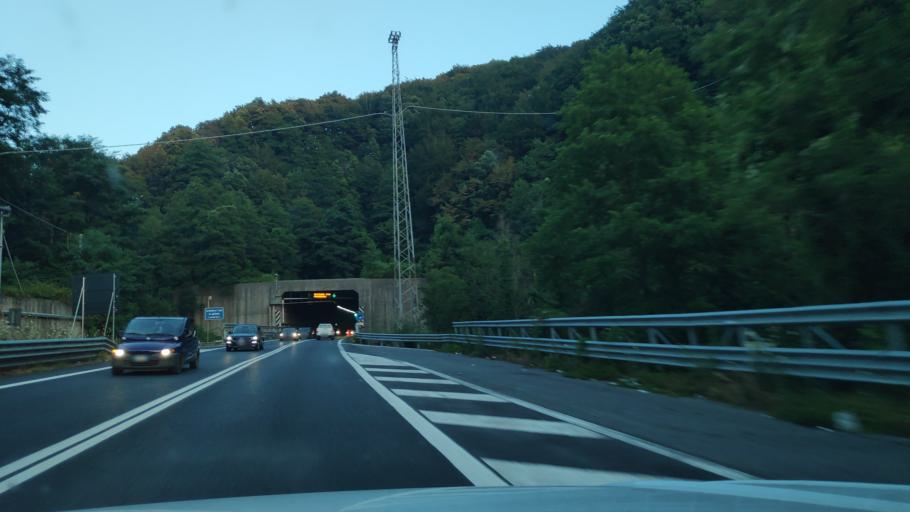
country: IT
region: Calabria
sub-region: Provincia di Reggio Calabria
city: Amato
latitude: 38.4018
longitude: 16.1626
